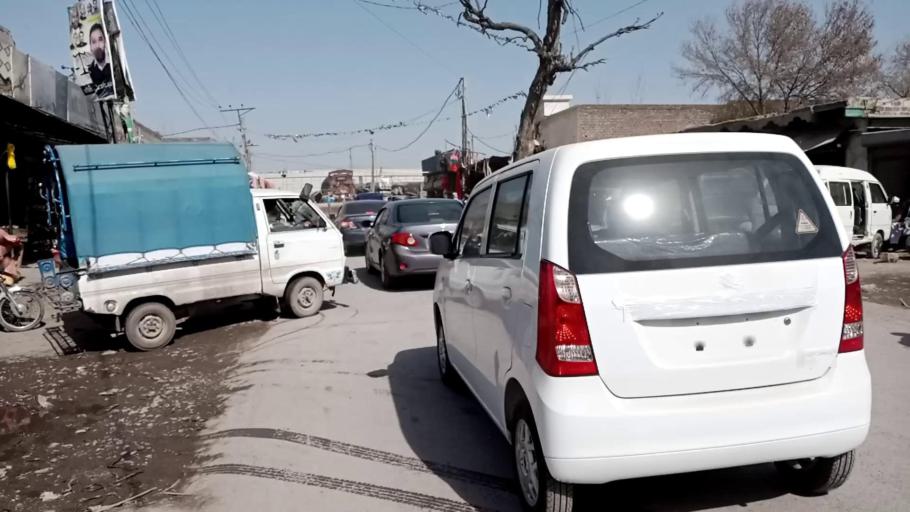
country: PK
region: Khyber Pakhtunkhwa
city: Peshawar
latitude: 34.0183
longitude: 71.6467
